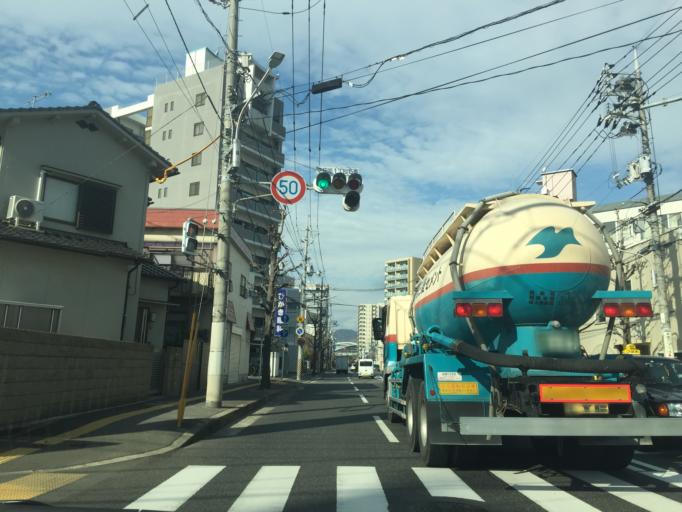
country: JP
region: Hiroshima
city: Hiroshima-shi
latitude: 34.4119
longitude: 132.4703
